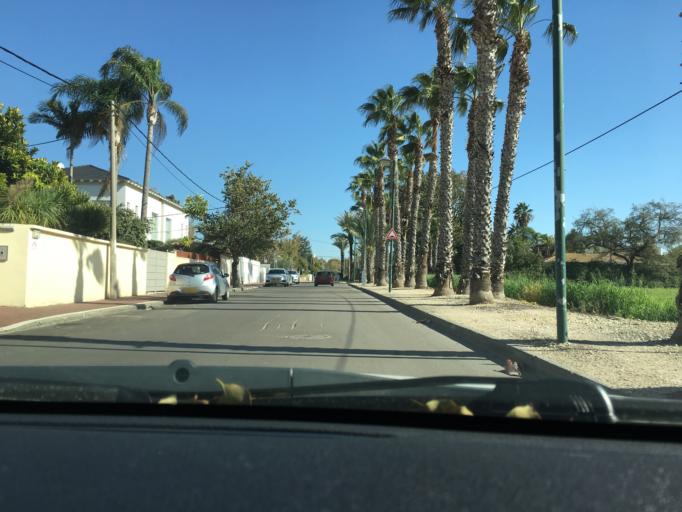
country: IL
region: Tel Aviv
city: Ramat HaSharon
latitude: 32.1477
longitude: 34.8310
